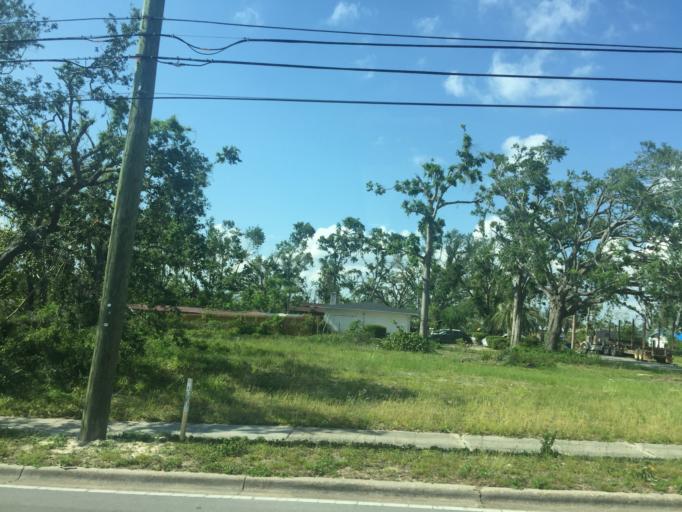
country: US
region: Florida
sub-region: Bay County
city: Cedar Grove
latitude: 30.1677
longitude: -85.6433
